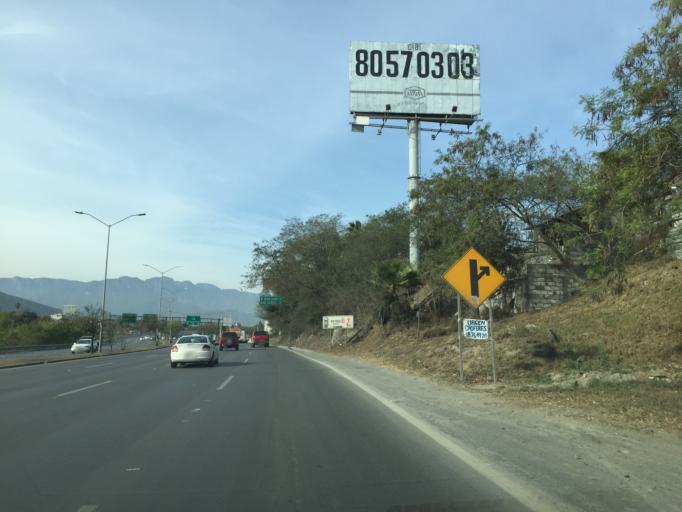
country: MX
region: Nuevo Leon
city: Guadalupe
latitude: 25.6927
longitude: -100.2153
